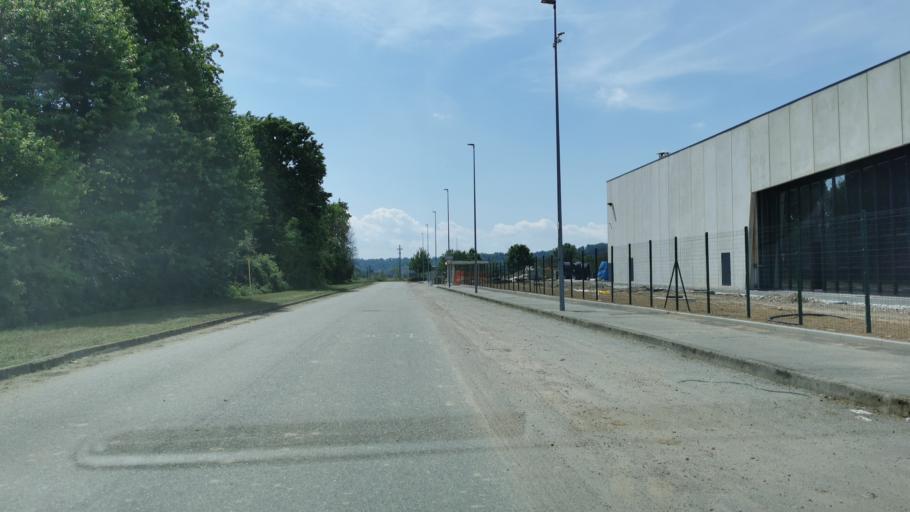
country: IT
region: Piedmont
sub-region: Provincia di Torino
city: Front
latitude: 45.3012
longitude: 7.6669
